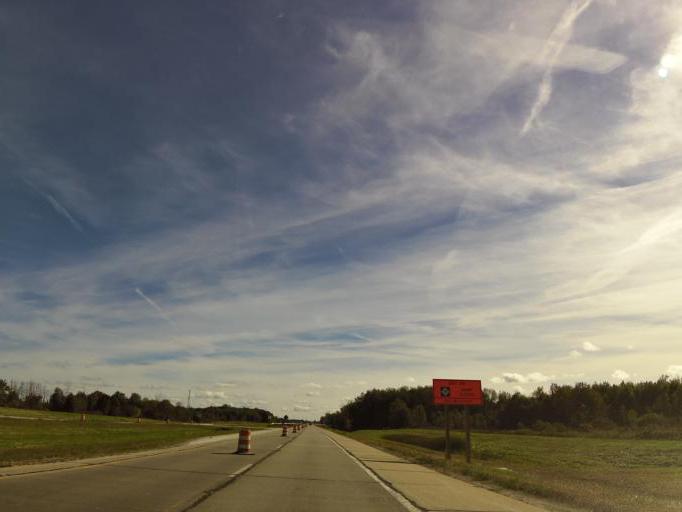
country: US
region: Michigan
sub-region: Macomb County
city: Memphis
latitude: 42.9784
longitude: -82.7846
